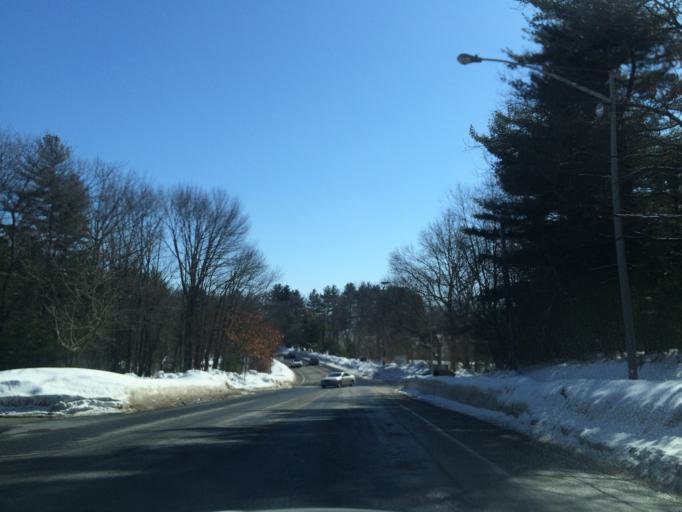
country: US
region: Massachusetts
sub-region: Norfolk County
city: Wellesley
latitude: 42.2915
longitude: -71.2702
